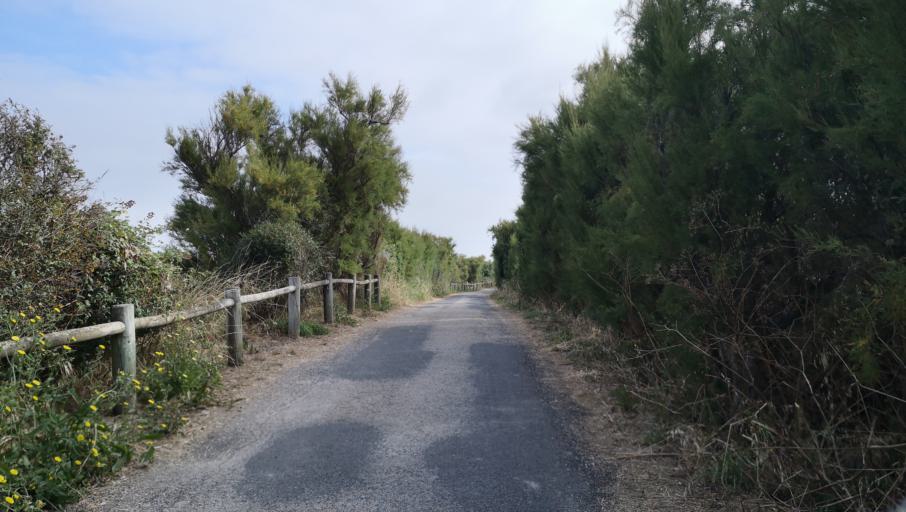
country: FR
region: Pays de la Loire
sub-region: Departement de la Vendee
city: Olonne-sur-Mer
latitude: 46.5389
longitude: -1.8034
